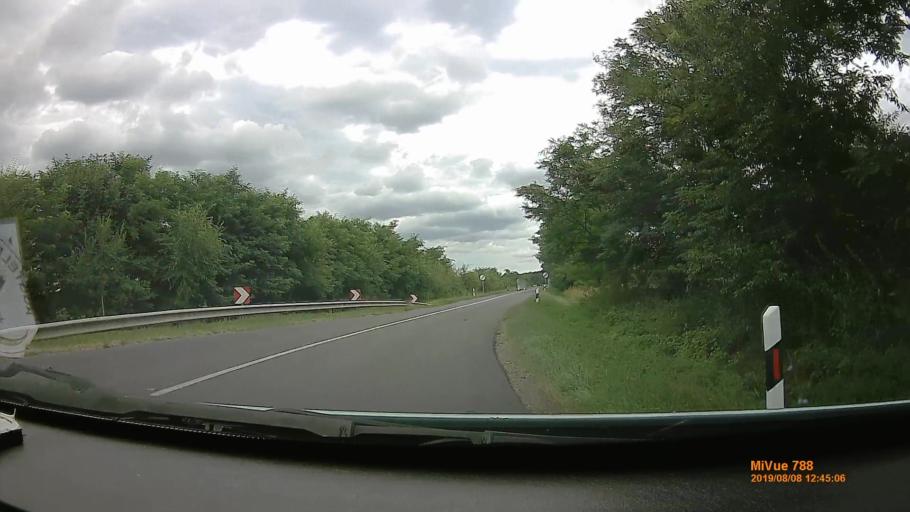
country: HU
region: Szabolcs-Szatmar-Bereg
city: Hodasz
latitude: 47.8903
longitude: 22.2025
